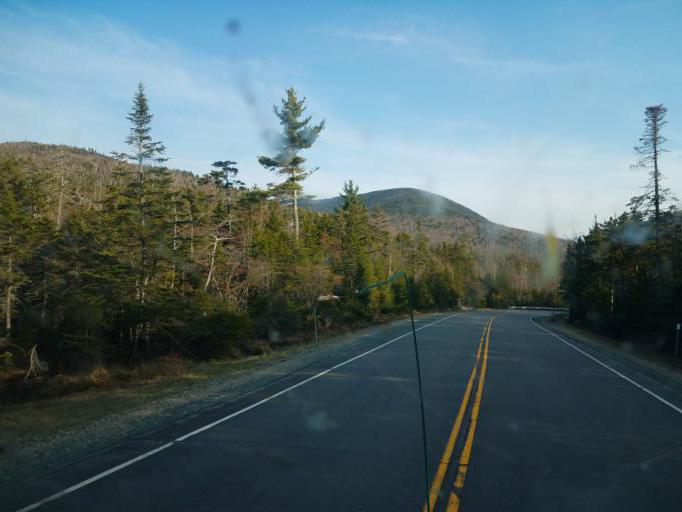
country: US
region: New Hampshire
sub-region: Grafton County
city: Woodstock
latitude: 44.0362
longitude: -71.5020
